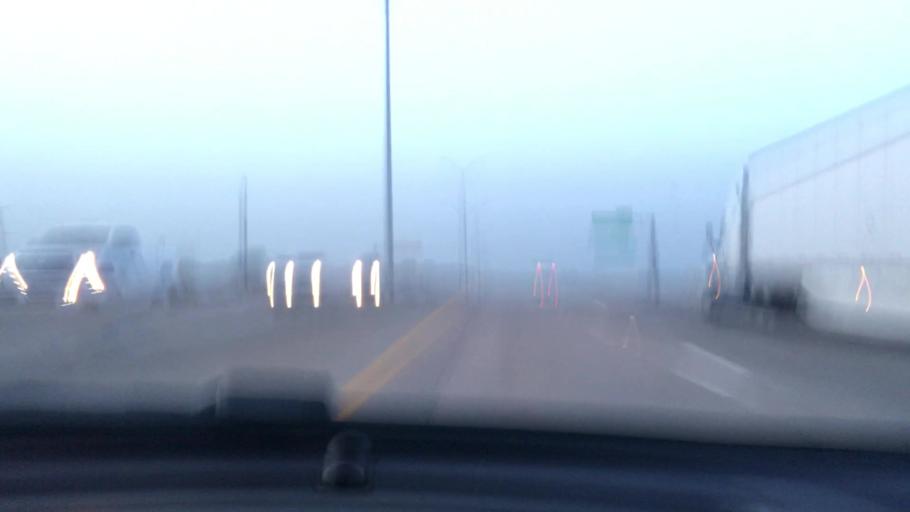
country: US
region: Texas
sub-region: Dallas County
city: DeSoto
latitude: 32.6348
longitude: -96.8233
